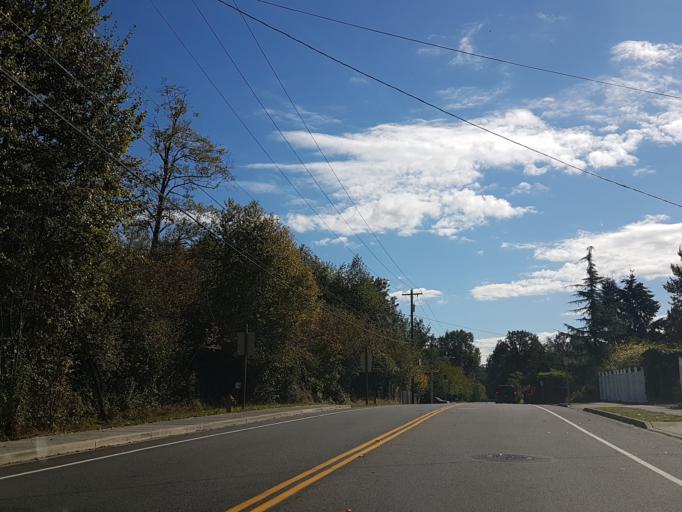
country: US
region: Washington
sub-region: Snohomish County
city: Brier
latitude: 47.7791
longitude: -122.2543
